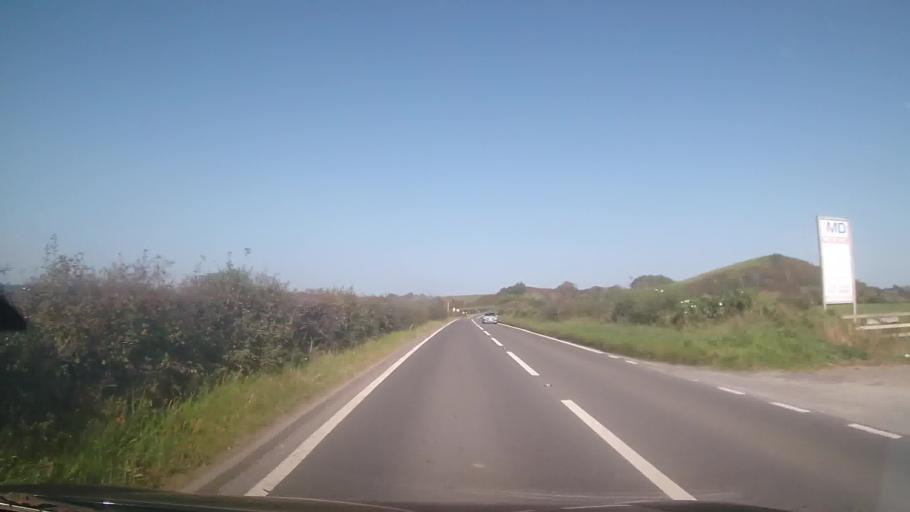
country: GB
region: Wales
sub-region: County of Ceredigion
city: Cardigan
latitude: 52.0950
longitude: -4.6299
